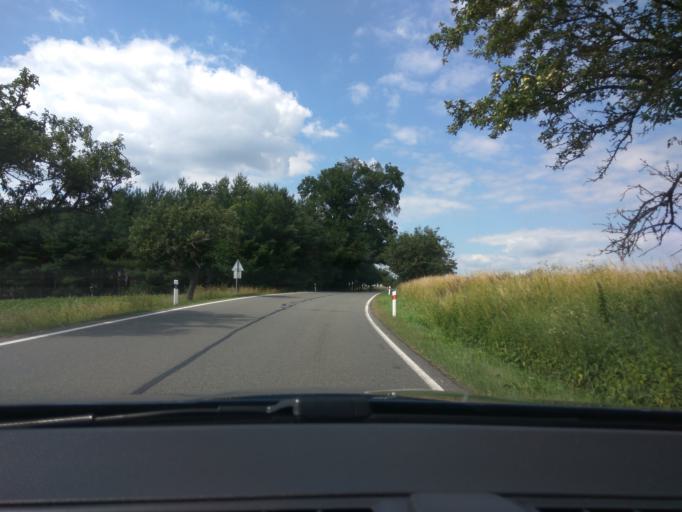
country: CZ
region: Jihocesky
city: Bernartice
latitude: 49.3992
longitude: 14.3633
